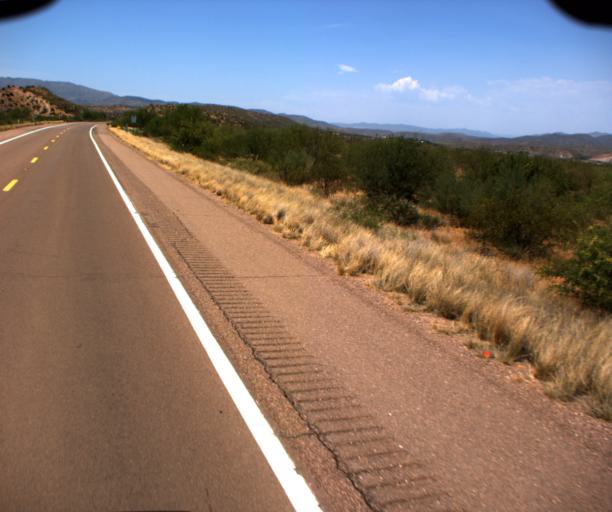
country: US
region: Arizona
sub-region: Gila County
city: Tonto Basin
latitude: 33.9132
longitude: -111.3132
